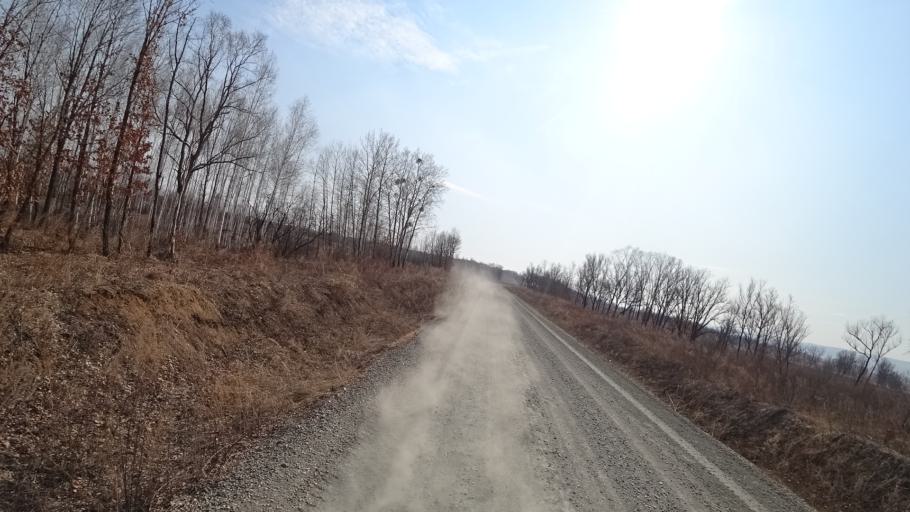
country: RU
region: Amur
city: Novobureyskiy
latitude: 49.8257
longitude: 129.9873
